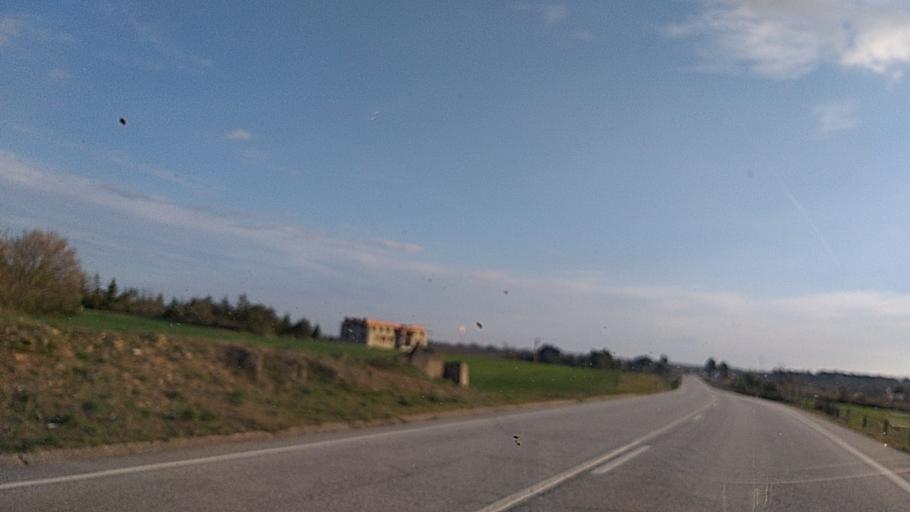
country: ES
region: Castille and Leon
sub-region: Provincia de Salamanca
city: Fuentes de Onoro
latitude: 40.6142
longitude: -6.9819
